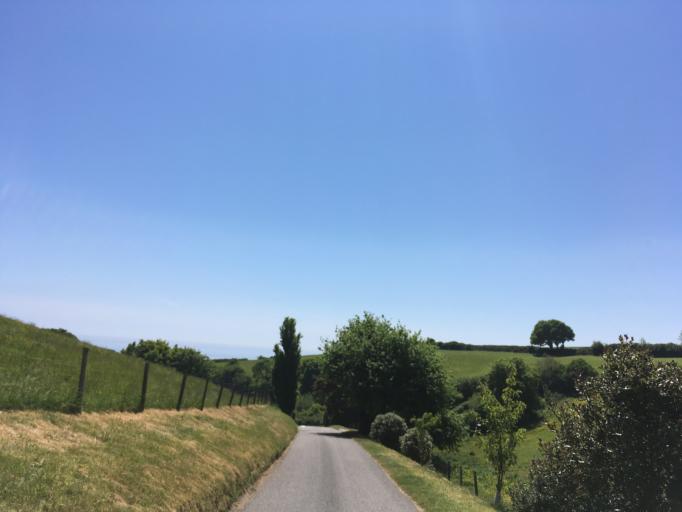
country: GB
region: England
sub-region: Devon
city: Dartmouth
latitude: 50.3487
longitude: -3.5371
